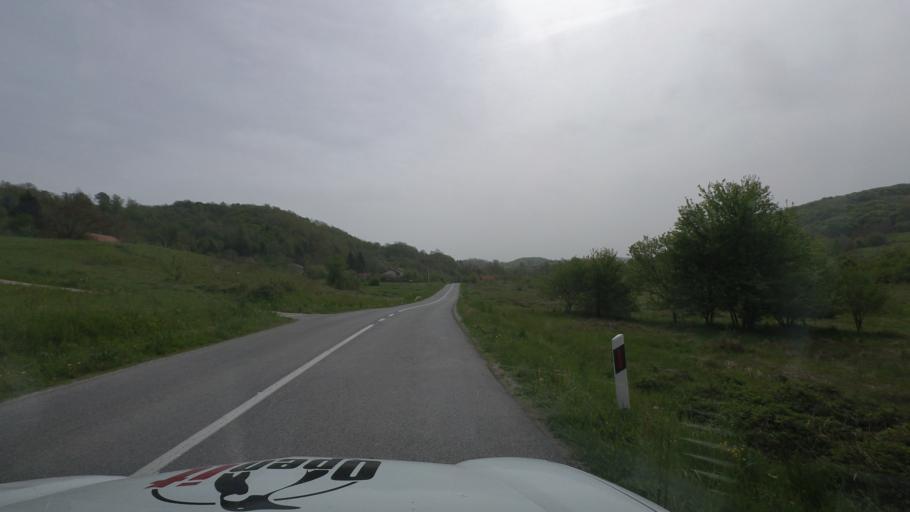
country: HR
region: Karlovacka
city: Vojnic
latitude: 45.3780
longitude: 15.6427
